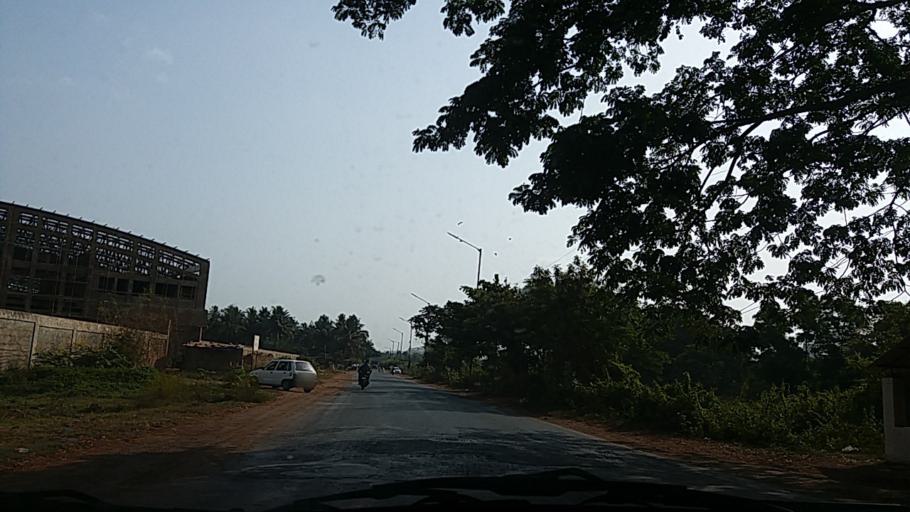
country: IN
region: Goa
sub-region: South Goa
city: Madgaon
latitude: 15.2601
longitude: 73.9685
